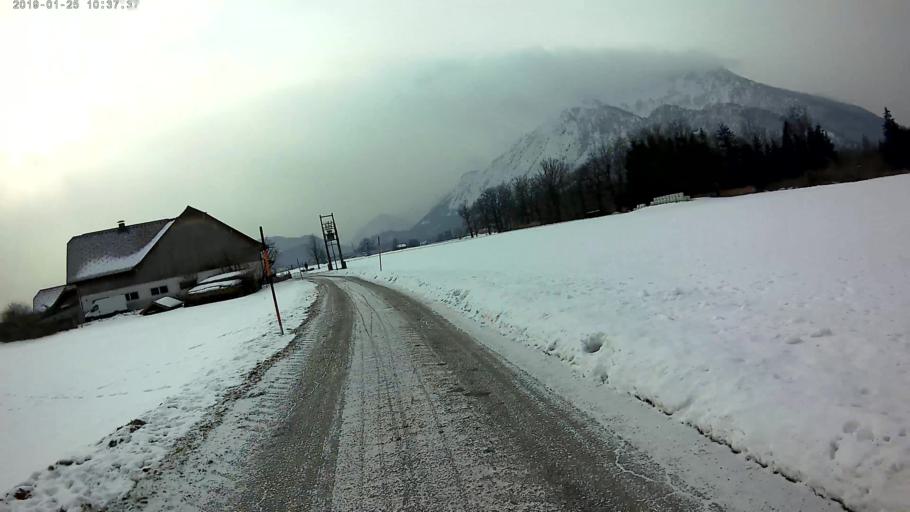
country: AT
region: Salzburg
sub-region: Politischer Bezirk Salzburg-Umgebung
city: Anif
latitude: 47.7567
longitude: 13.0502
